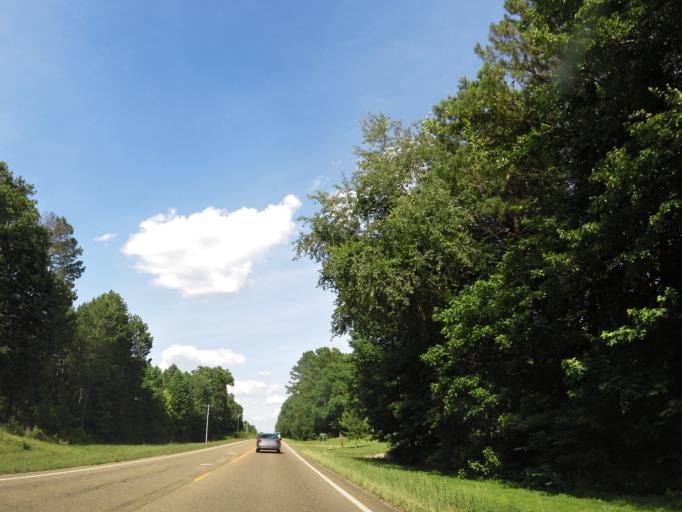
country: US
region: Tennessee
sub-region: Carroll County
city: Bruceton
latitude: 36.0333
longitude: -88.3298
